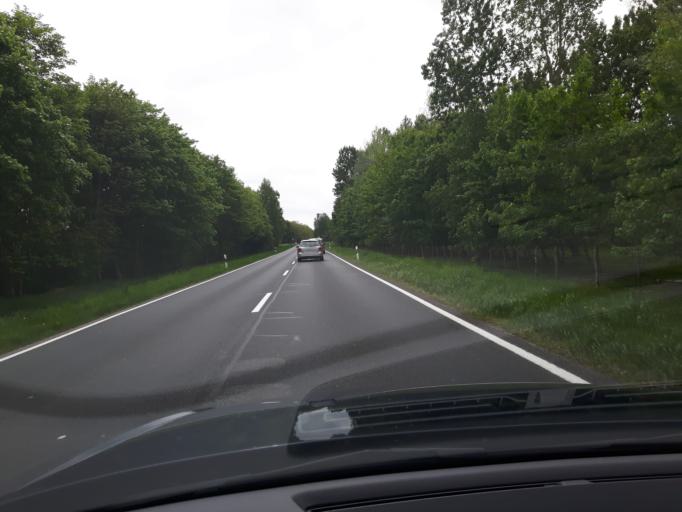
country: DE
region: Mecklenburg-Vorpommern
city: Ostseebad Dierhagen
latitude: 54.2331
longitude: 12.3642
